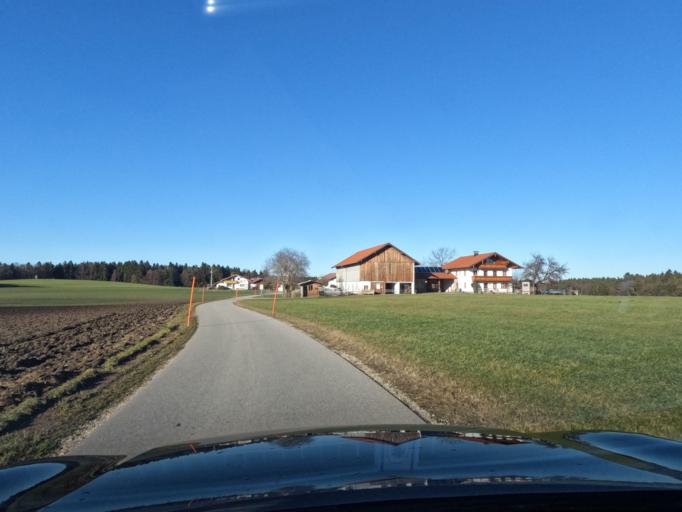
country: DE
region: Bavaria
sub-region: Upper Bavaria
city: Surberg
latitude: 47.8786
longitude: 12.6896
